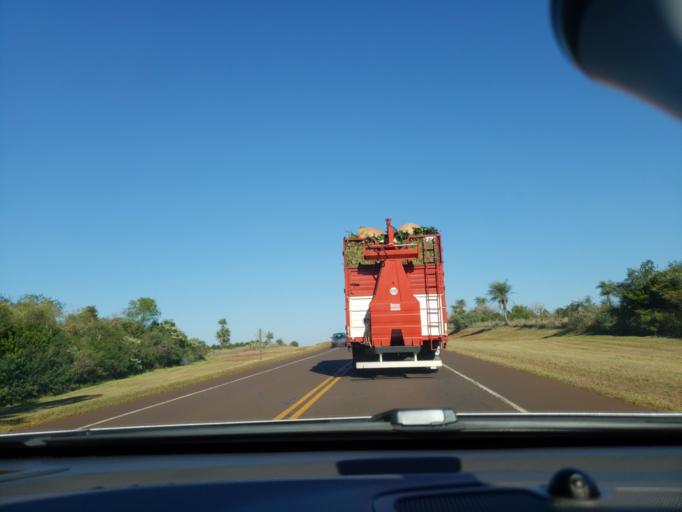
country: AR
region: Misiones
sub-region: Departamento de Apostoles
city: San Jose
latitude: -27.8354
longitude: -55.7691
